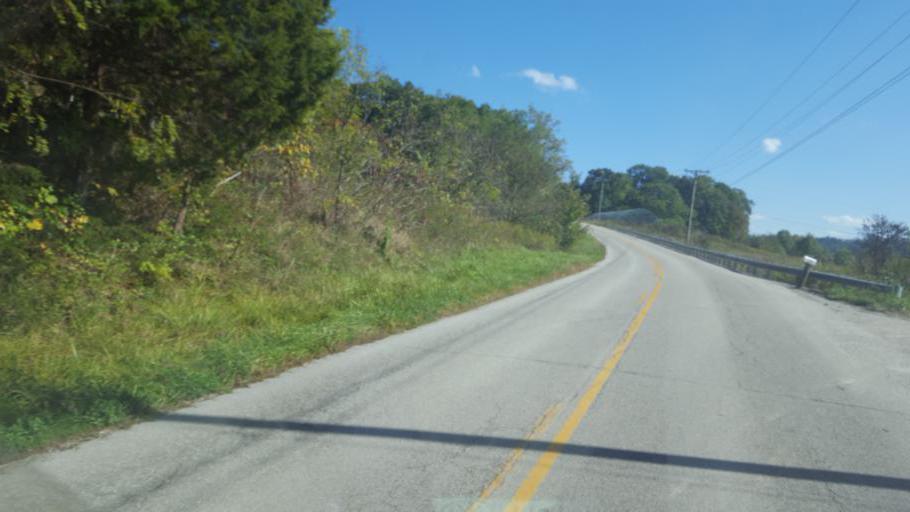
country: US
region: Kentucky
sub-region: Fleming County
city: Flemingsburg
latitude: 38.4677
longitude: -83.5759
